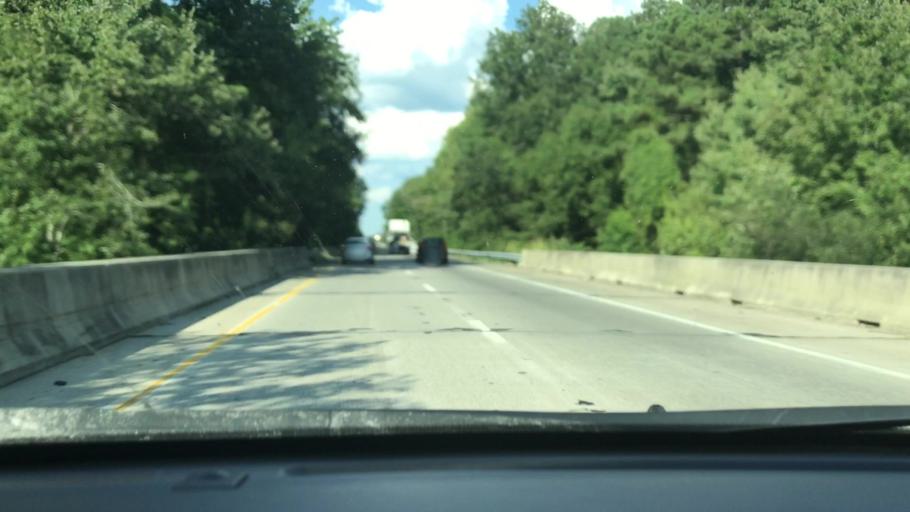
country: US
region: South Carolina
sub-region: Dillon County
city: Latta
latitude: 34.3128
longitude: -79.6068
